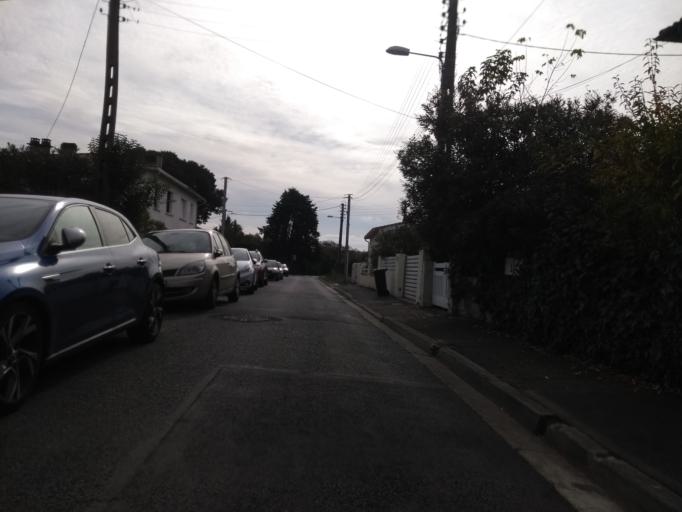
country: FR
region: Aquitaine
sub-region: Departement de la Gironde
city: Talence
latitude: 44.8115
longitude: -0.5958
